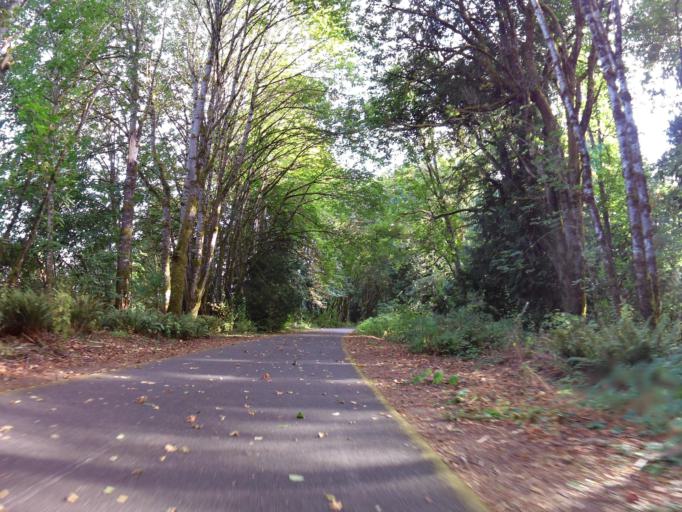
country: US
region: Washington
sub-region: Thurston County
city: Lacey
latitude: 47.0053
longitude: -122.8323
